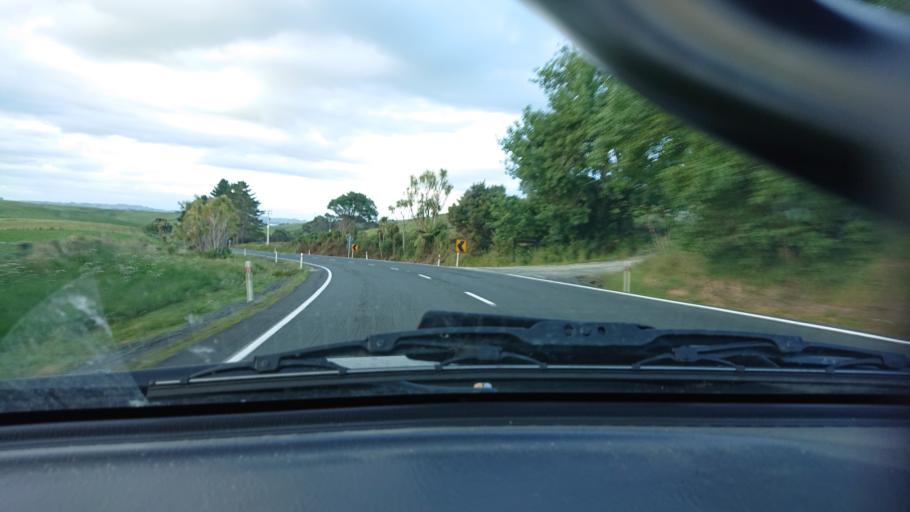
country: NZ
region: Auckland
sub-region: Auckland
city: Parakai
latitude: -36.4716
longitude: 174.4497
